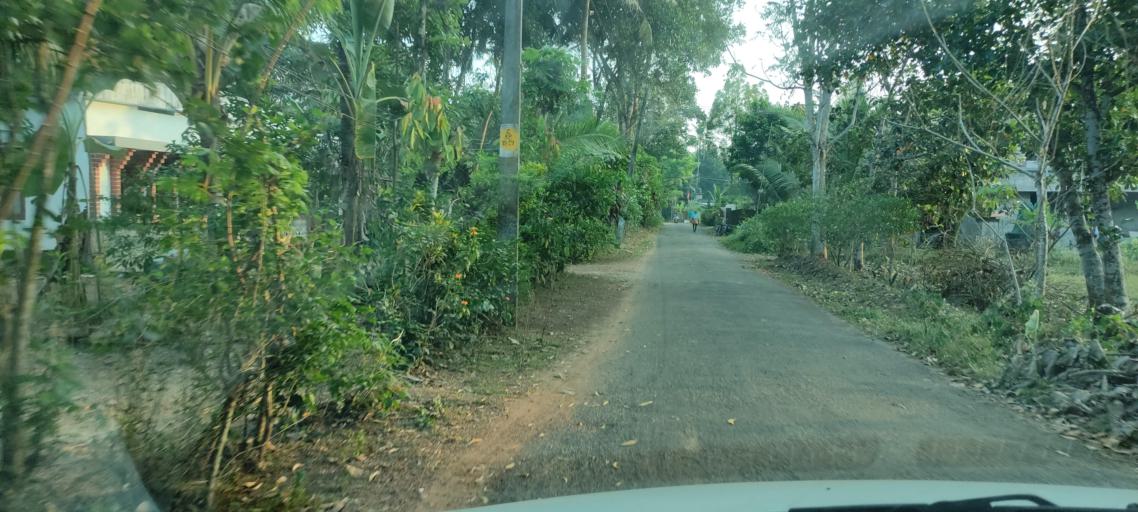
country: IN
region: Kerala
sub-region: Alappuzha
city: Kattanam
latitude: 9.1686
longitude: 76.5911
